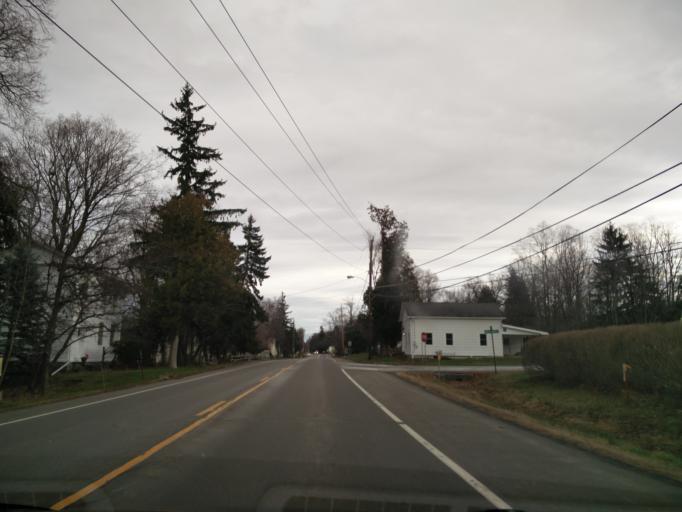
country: US
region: New York
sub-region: Tompkins County
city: Trumansburg
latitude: 42.5108
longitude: -76.6176
